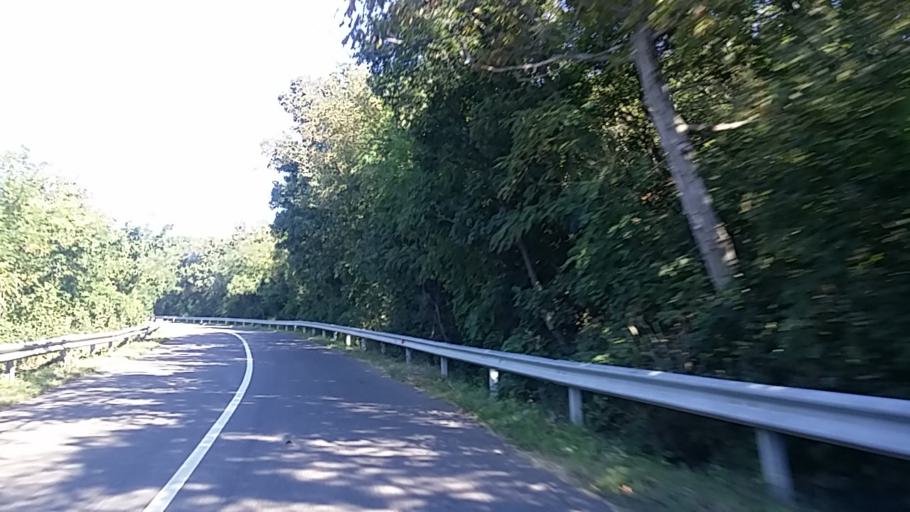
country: HU
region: Nograd
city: Paszto
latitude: 47.9228
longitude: 19.6186
